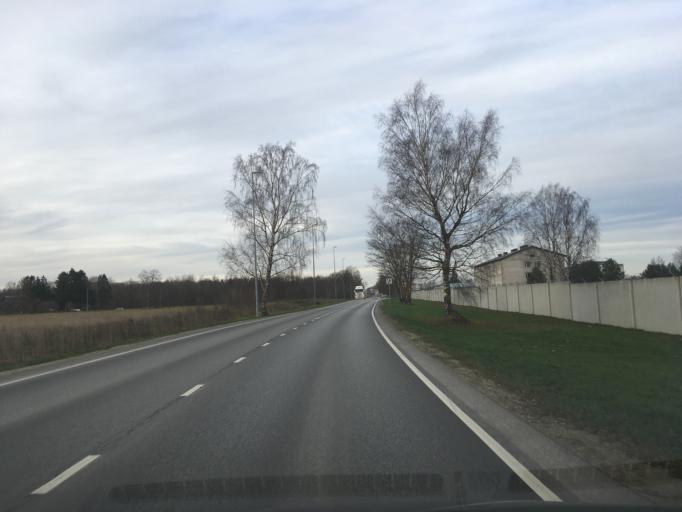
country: EE
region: Ida-Virumaa
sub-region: Johvi vald
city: Johvi
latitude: 59.3470
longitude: 27.4365
